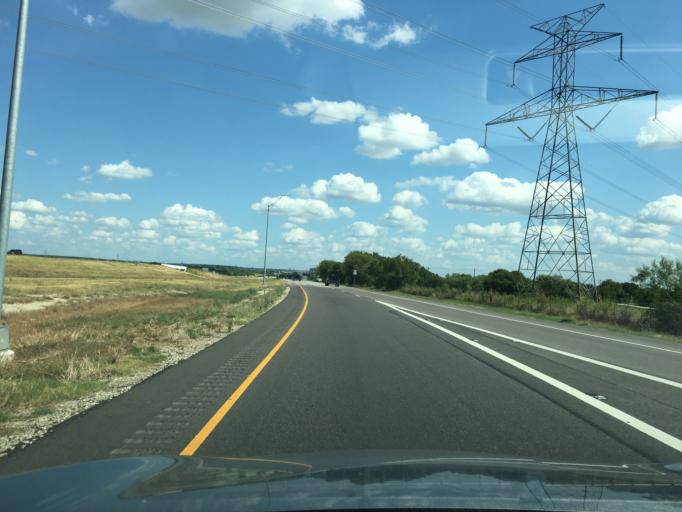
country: US
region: Texas
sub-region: Tarrant County
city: Mansfield
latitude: 32.5179
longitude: -97.0764
